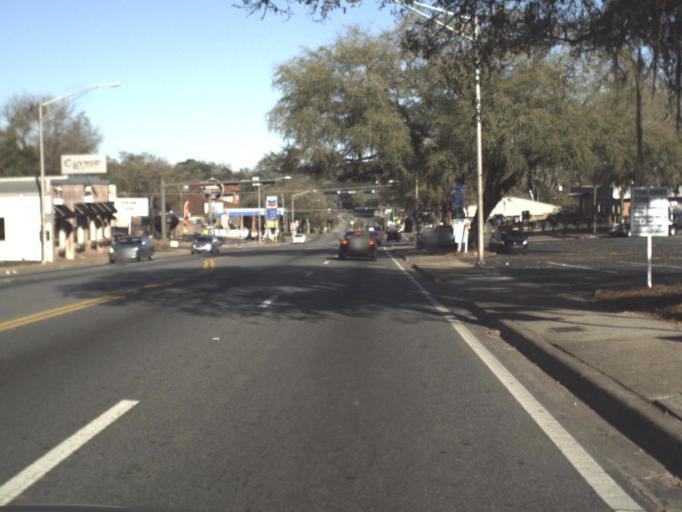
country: US
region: Florida
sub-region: Leon County
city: Tallahassee
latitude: 30.4447
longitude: -84.2794
